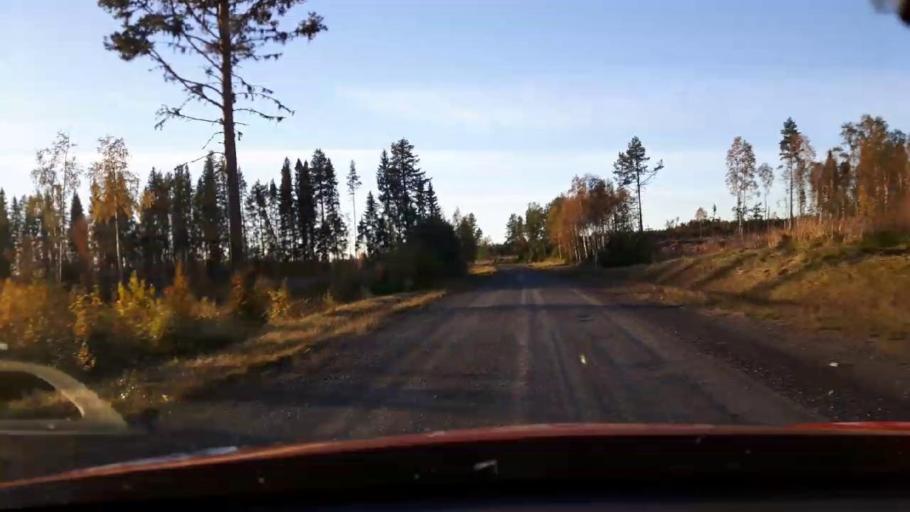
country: SE
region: Jaemtland
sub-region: Krokoms Kommun
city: Krokom
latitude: 63.4381
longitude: 14.6033
